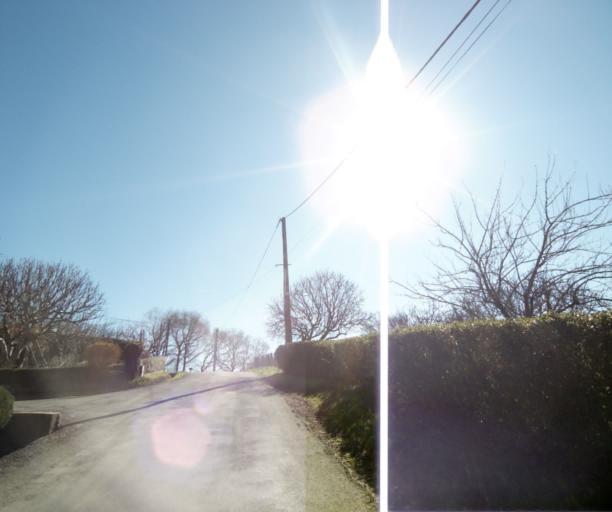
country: FR
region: Aquitaine
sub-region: Departement des Pyrenees-Atlantiques
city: Urrugne
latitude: 43.3452
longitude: -1.6800
